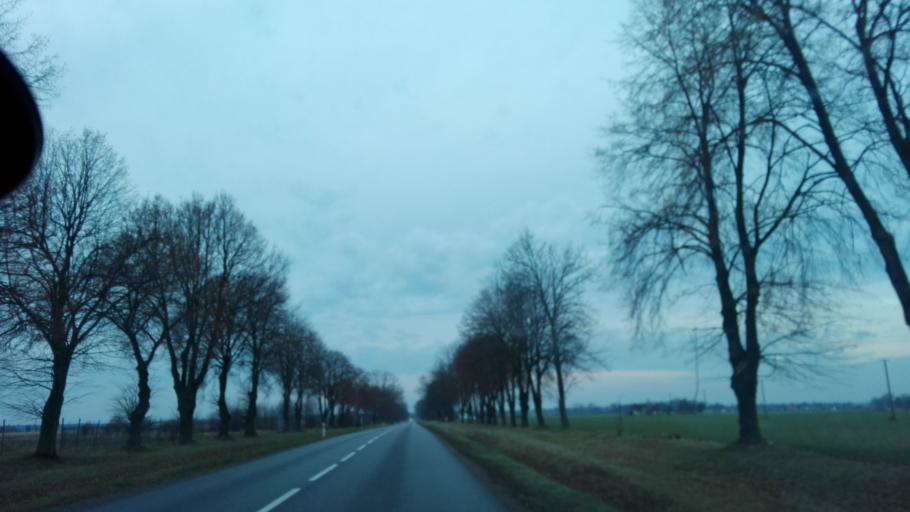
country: PL
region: Lublin Voivodeship
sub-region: Powiat radzynski
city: Wohyn
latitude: 51.7792
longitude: 22.7852
